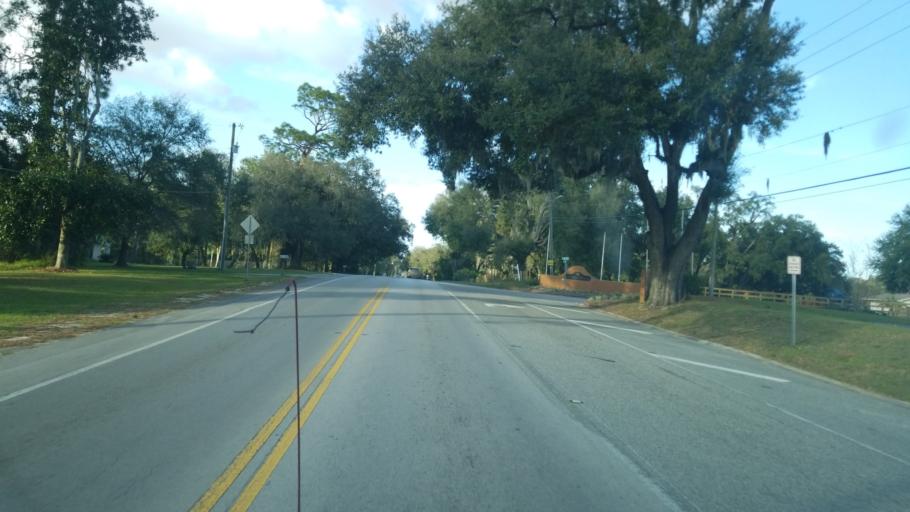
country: US
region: Florida
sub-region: Marion County
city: Ocala
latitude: 29.2673
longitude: -82.1117
